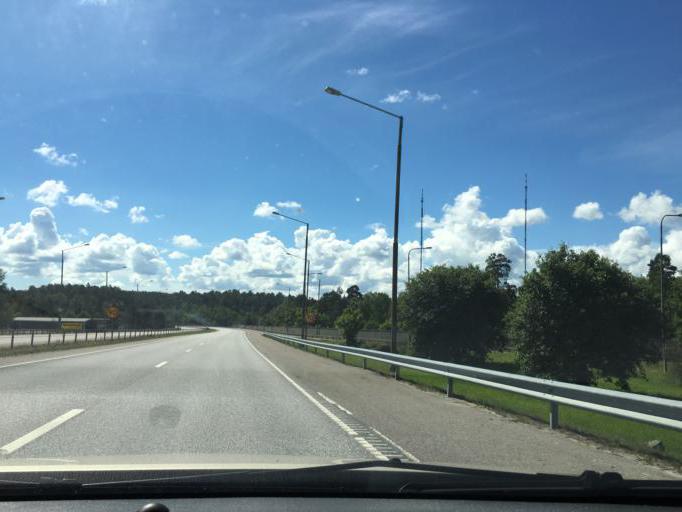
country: SE
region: Stockholm
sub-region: Nacka Kommun
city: Nacka
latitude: 59.3086
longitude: 18.1805
